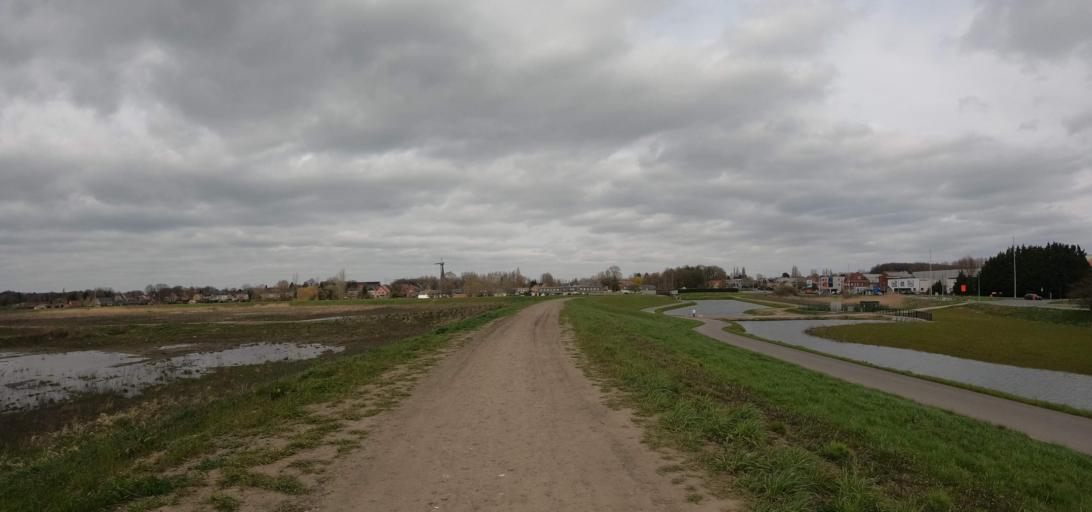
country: BE
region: Flanders
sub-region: Provincie Oost-Vlaanderen
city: Hamme
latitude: 51.1091
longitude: 4.1406
